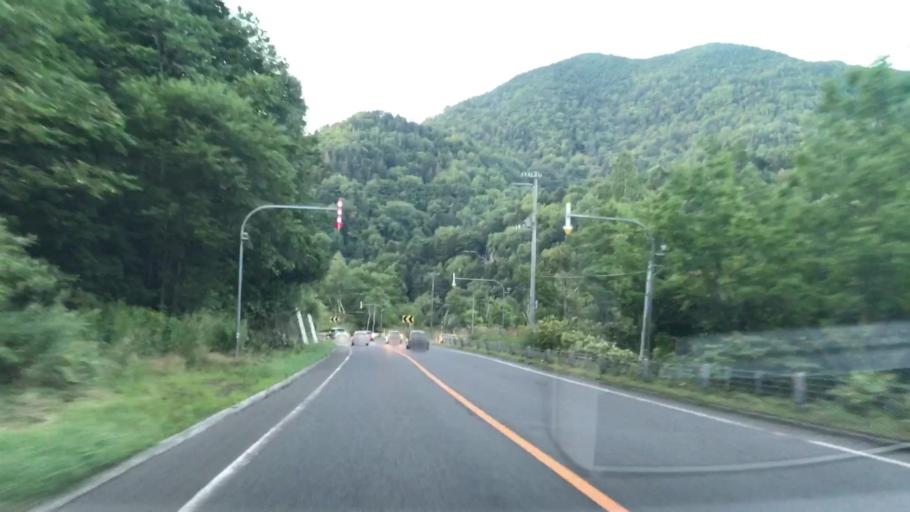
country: JP
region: Hokkaido
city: Sapporo
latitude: 42.9185
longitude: 141.1250
